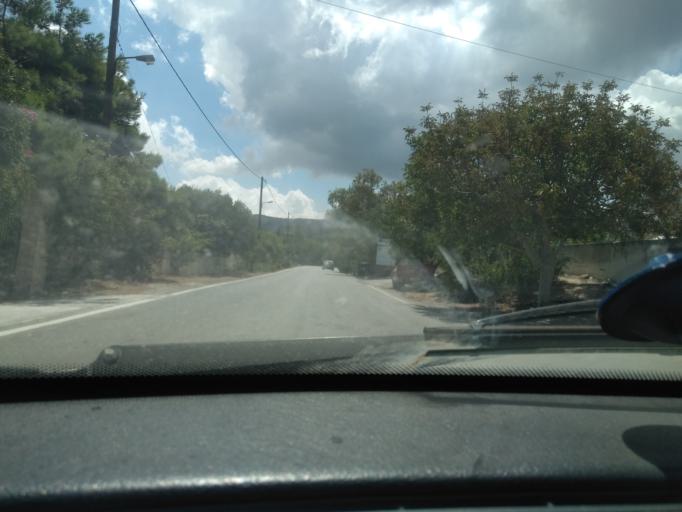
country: GR
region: Crete
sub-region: Nomos Lasithiou
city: Makry-Gialos
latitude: 35.1038
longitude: 26.0597
